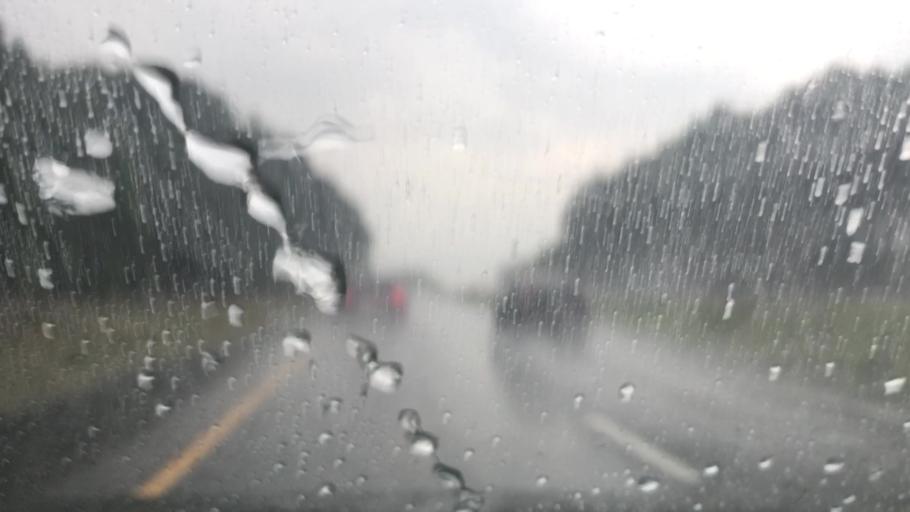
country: US
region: New Jersey
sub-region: Monmouth County
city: Tinton Falls
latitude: 40.2755
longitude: -74.0815
